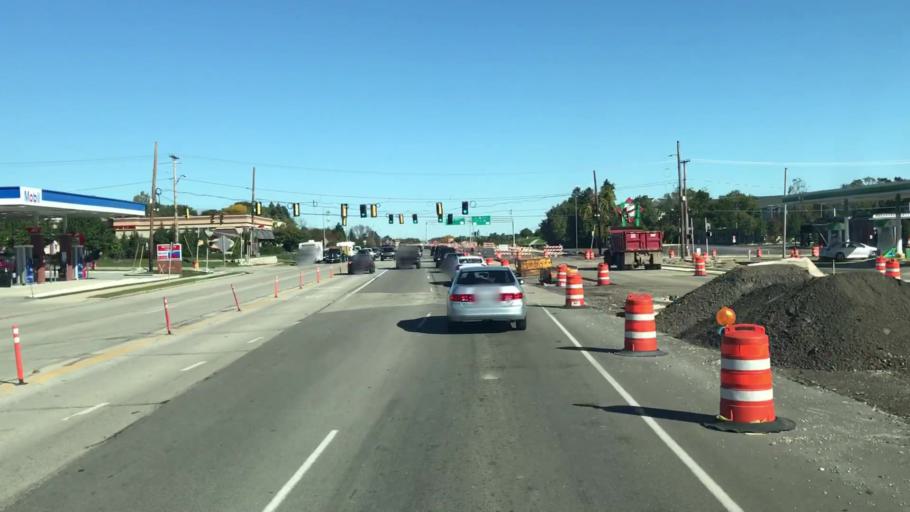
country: US
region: Wisconsin
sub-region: Milwaukee County
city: Hales Corners
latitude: 42.9510
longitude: -88.0481
